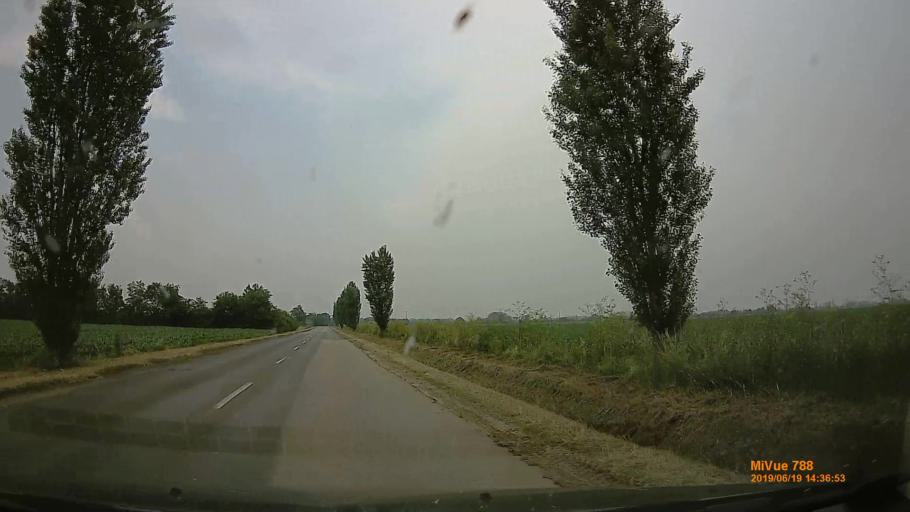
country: HU
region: Baranya
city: Szigetvar
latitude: 46.0591
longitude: 17.7768
